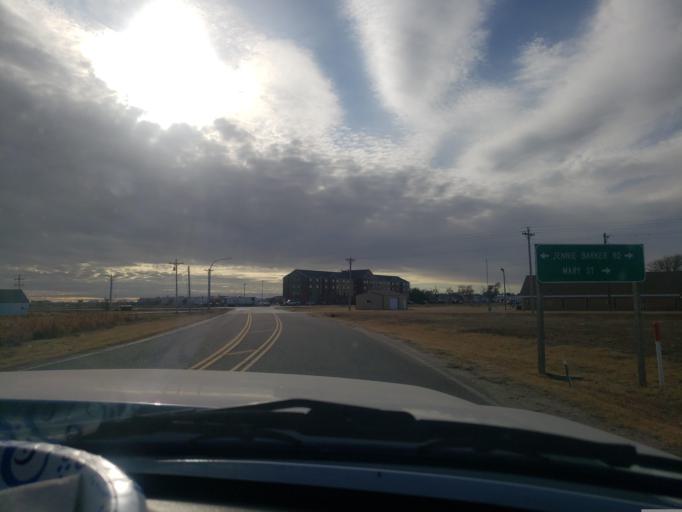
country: US
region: Kansas
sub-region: Finney County
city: Garden City
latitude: 37.9890
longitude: -100.8280
